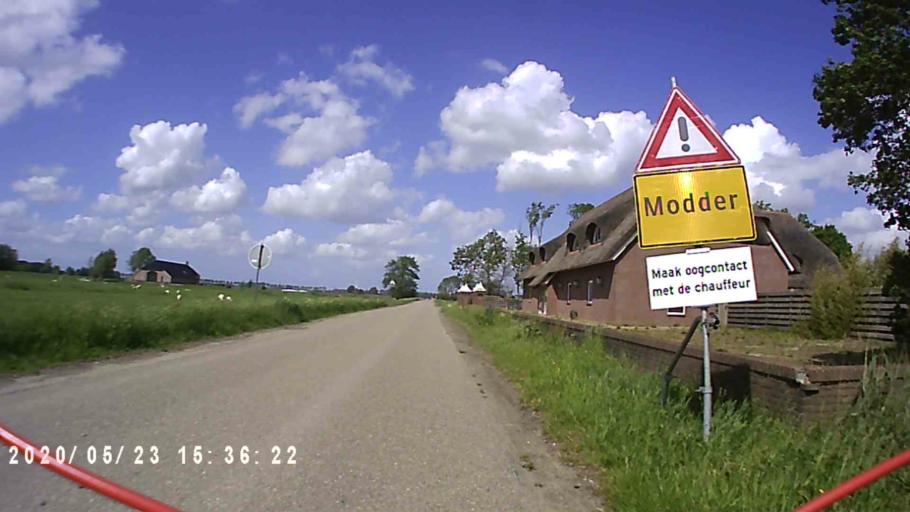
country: NL
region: Groningen
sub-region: Gemeente Delfzijl
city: Delfzijl
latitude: 53.2694
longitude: 6.9389
